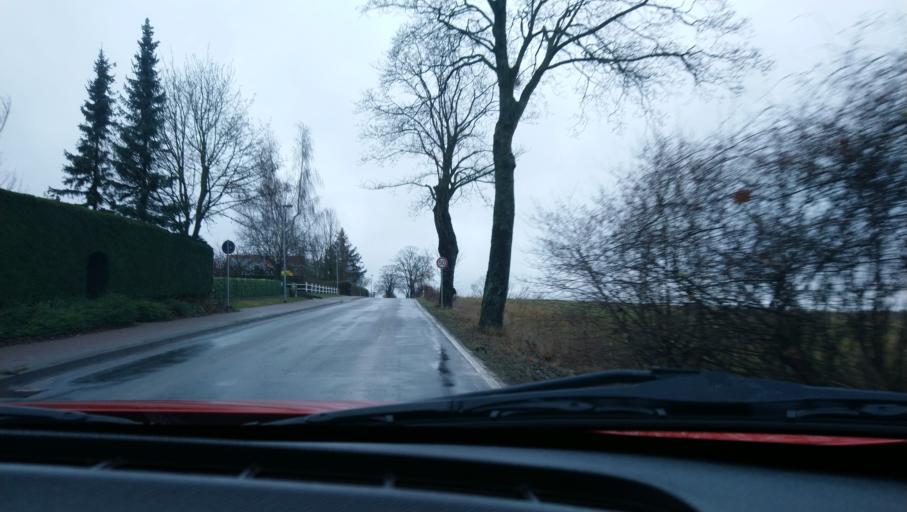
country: DE
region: Mecklenburg-Vorpommern
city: Seehof
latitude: 53.6856
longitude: 11.4298
